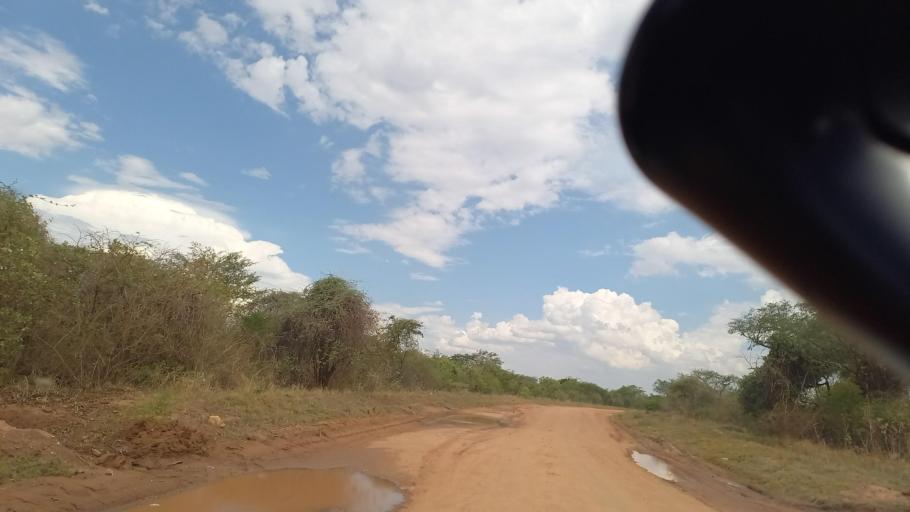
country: ZM
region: Southern
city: Nakambala
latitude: -16.0509
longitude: 27.9839
